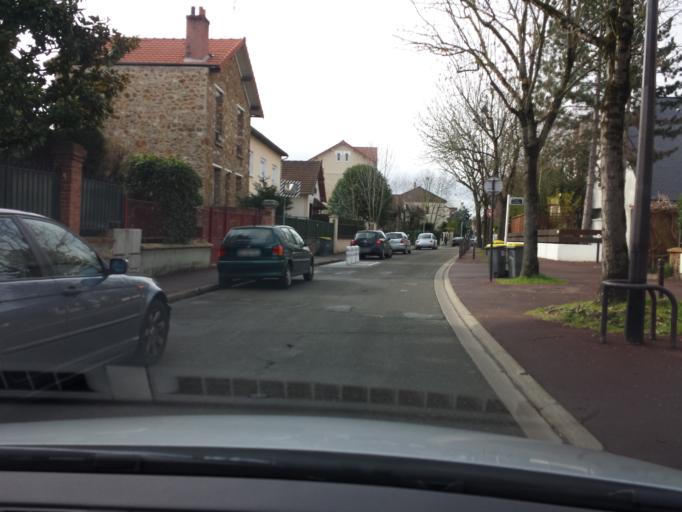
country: FR
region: Ile-de-France
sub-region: Departement des Hauts-de-Seine
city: Antony
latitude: 48.7521
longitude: 2.2912
